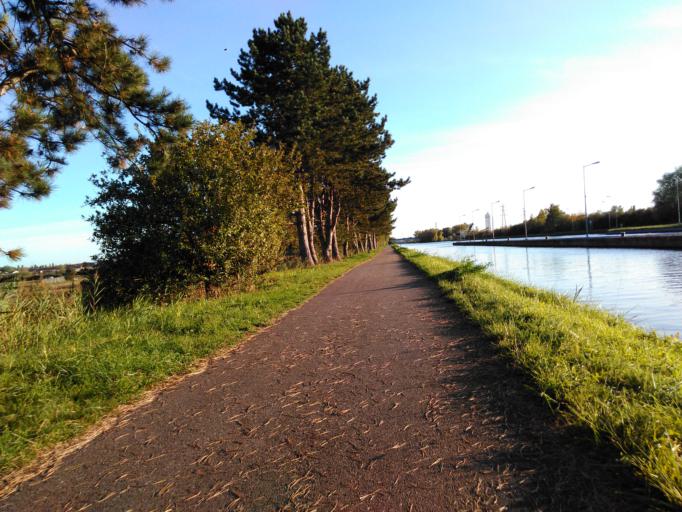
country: FR
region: Lorraine
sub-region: Departement de la Moselle
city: Talange
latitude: 49.2263
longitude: 6.1835
